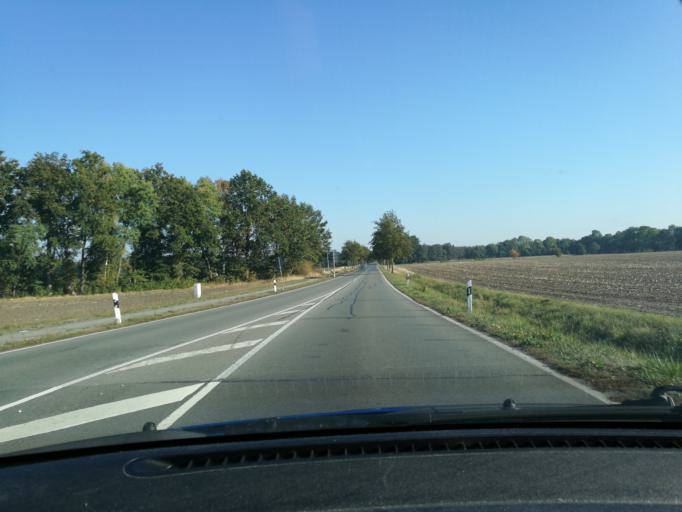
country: DE
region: Lower Saxony
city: Dannenberg
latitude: 53.1009
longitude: 11.0589
